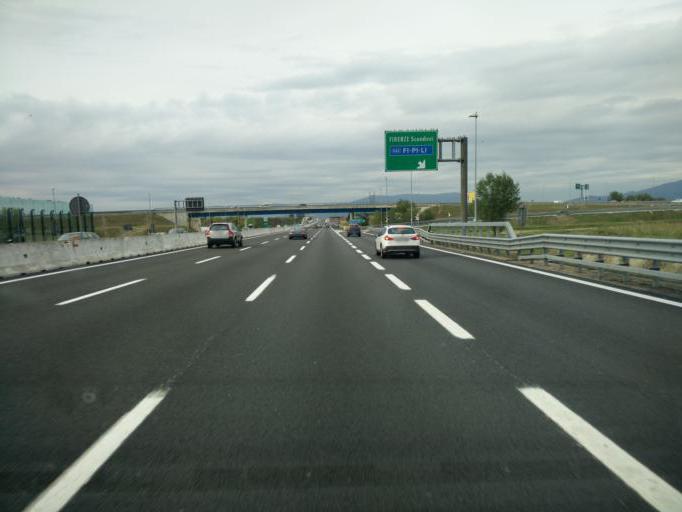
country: IT
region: Tuscany
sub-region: Province of Florence
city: Mantignano-Ugnano
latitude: 43.7759
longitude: 11.1619
